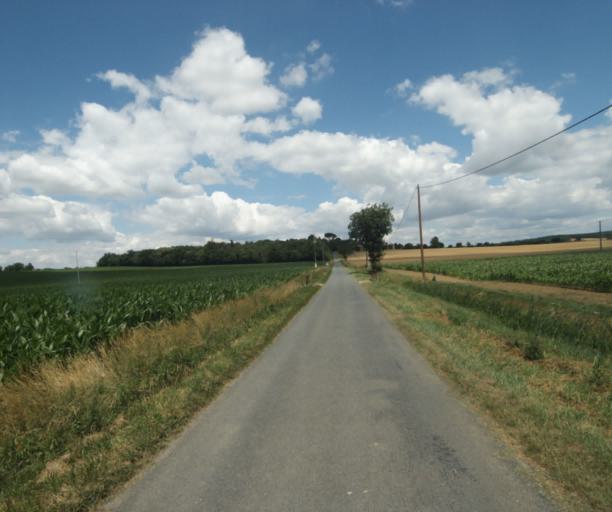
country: FR
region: Midi-Pyrenees
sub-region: Departement du Tarn
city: Puylaurens
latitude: 43.5206
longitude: 2.0226
